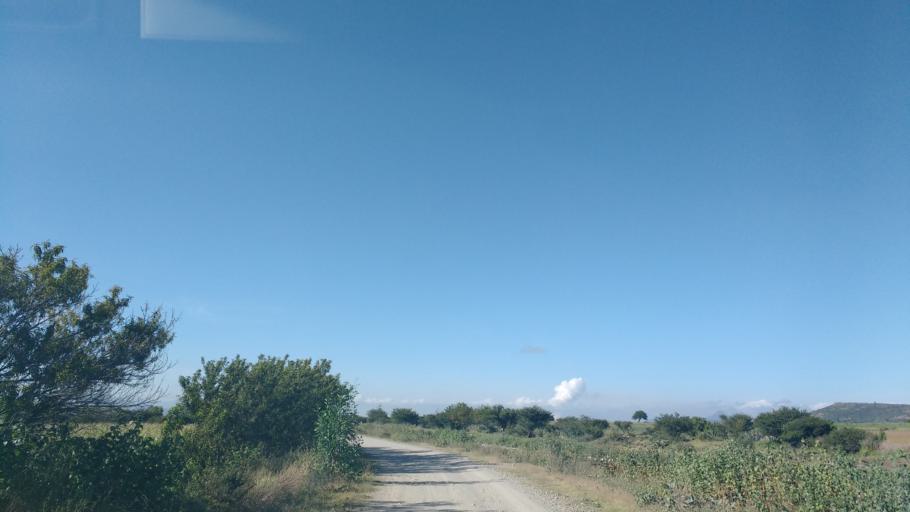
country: MX
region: Hidalgo
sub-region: Tezontepec de Aldama
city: Tenango
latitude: 20.2524
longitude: -99.2545
